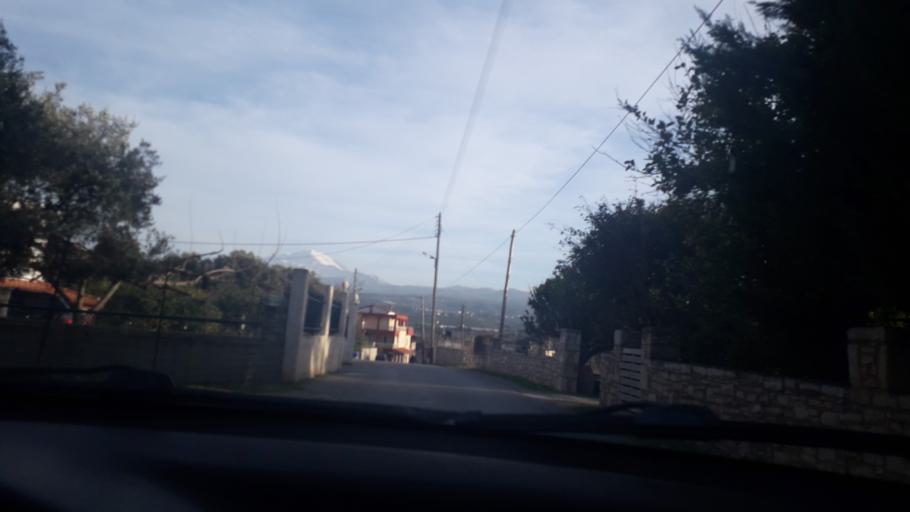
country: GR
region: Crete
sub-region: Nomos Rethymnis
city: Panormos
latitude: 35.3845
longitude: 24.6185
